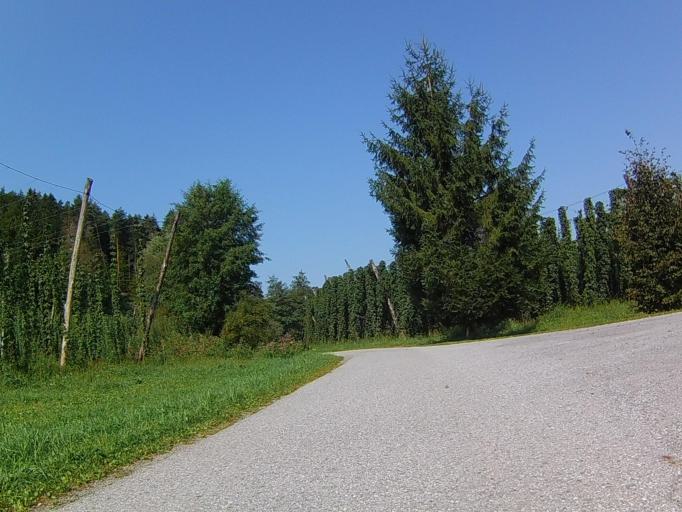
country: AT
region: Styria
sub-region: Politischer Bezirk Leibnitz
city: Leutschach
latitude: 46.6652
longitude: 15.4552
